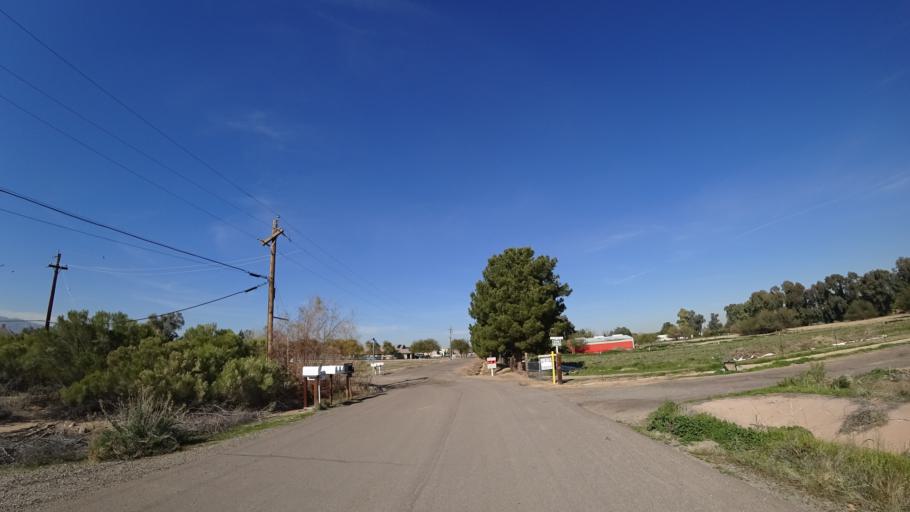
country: US
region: Arizona
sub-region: Maricopa County
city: Citrus Park
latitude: 33.5261
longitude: -112.4354
